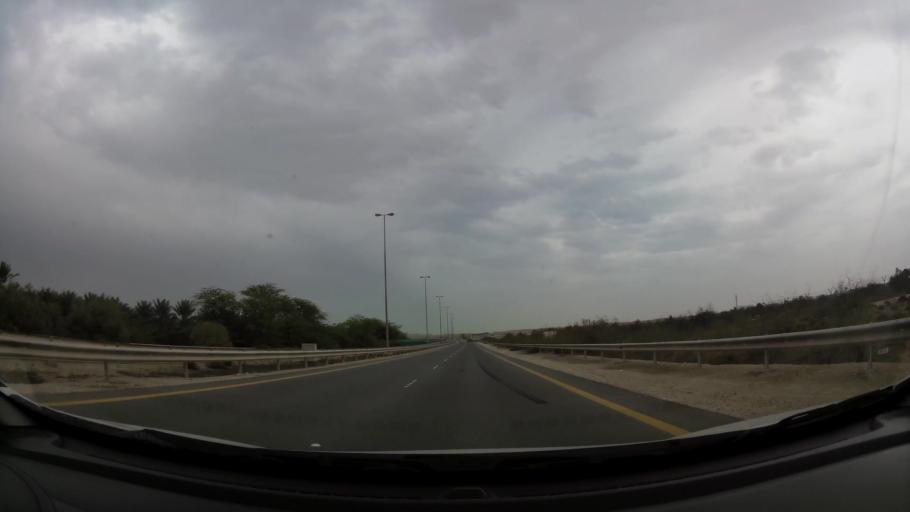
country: BH
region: Central Governorate
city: Dar Kulayb
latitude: 26.0197
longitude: 50.5020
